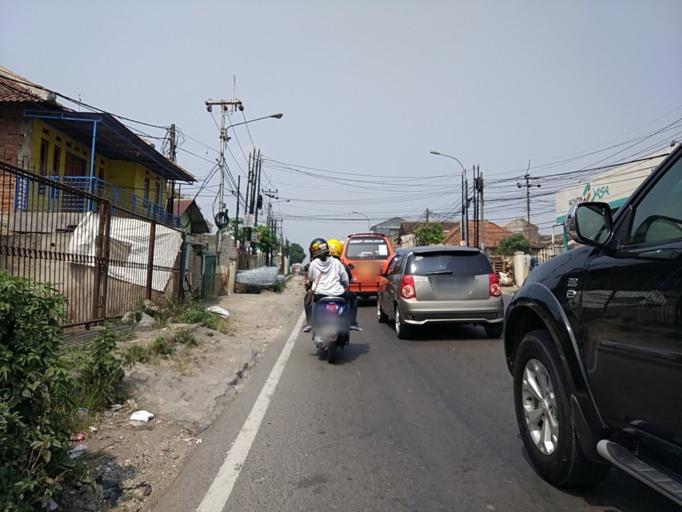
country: ID
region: West Java
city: Padalarang
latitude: -6.8539
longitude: 107.4979
